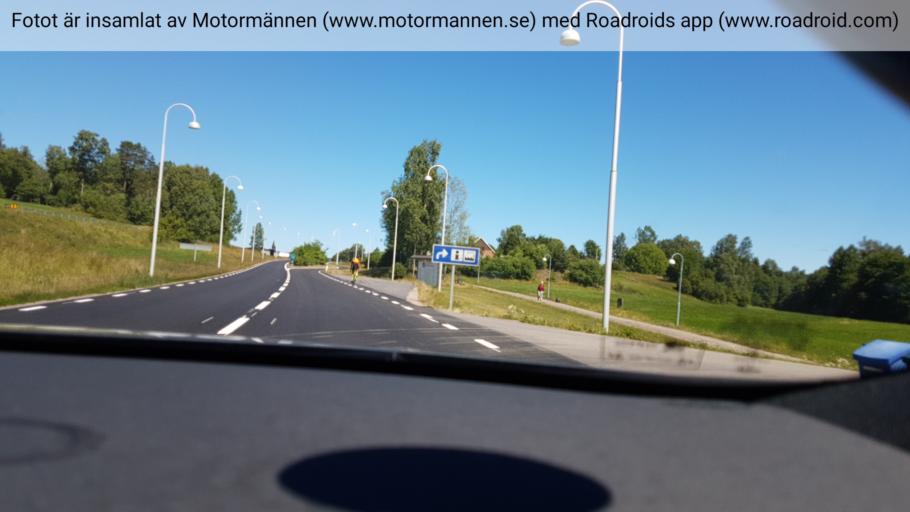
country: SE
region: Vaestra Goetaland
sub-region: Ulricehamns Kommun
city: Ulricehamn
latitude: 57.9186
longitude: 13.4862
